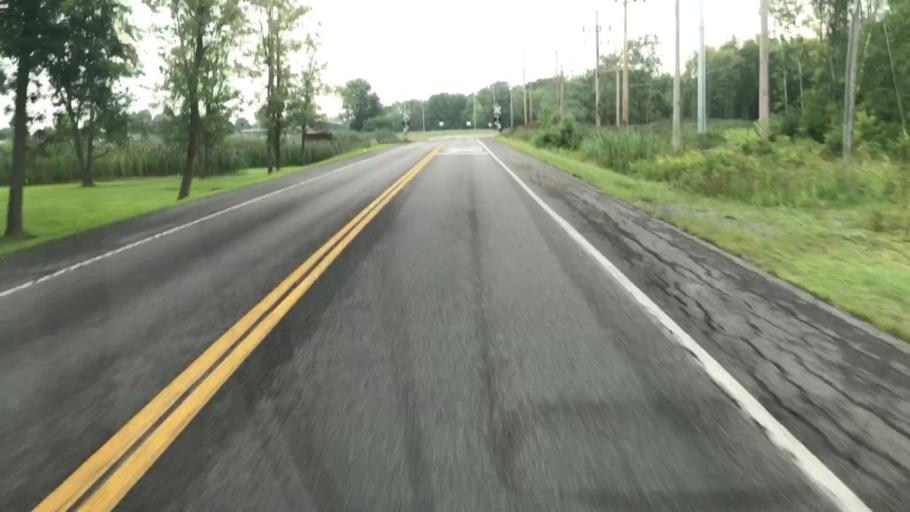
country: US
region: New York
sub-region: Onondaga County
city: Liverpool
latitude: 43.1535
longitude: -76.1899
